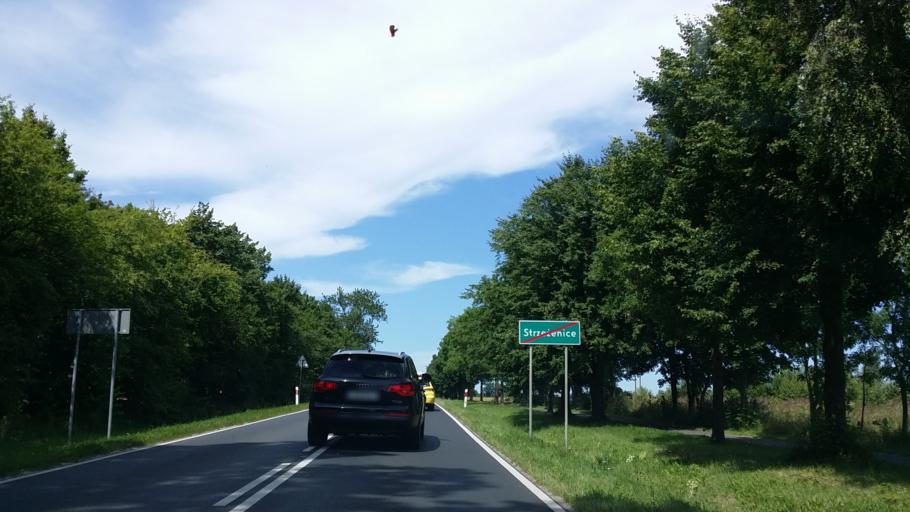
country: PL
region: West Pomeranian Voivodeship
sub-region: Powiat koszalinski
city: Mielno
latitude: 54.2416
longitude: 16.0682
